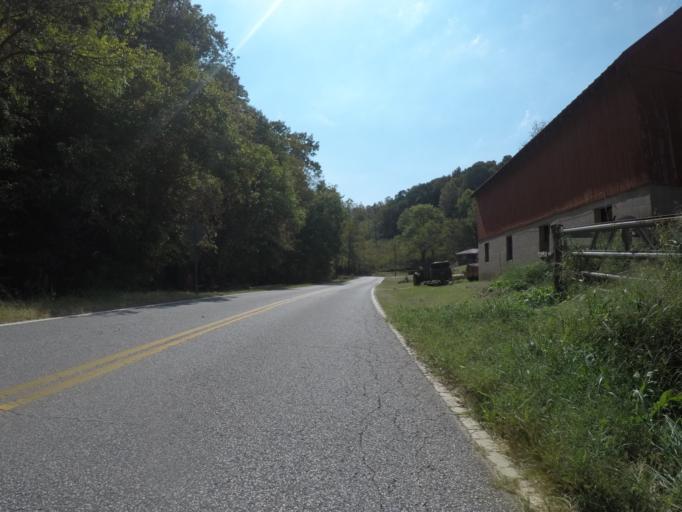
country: US
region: West Virginia
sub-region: Cabell County
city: Lesage
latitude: 38.5812
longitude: -82.4181
